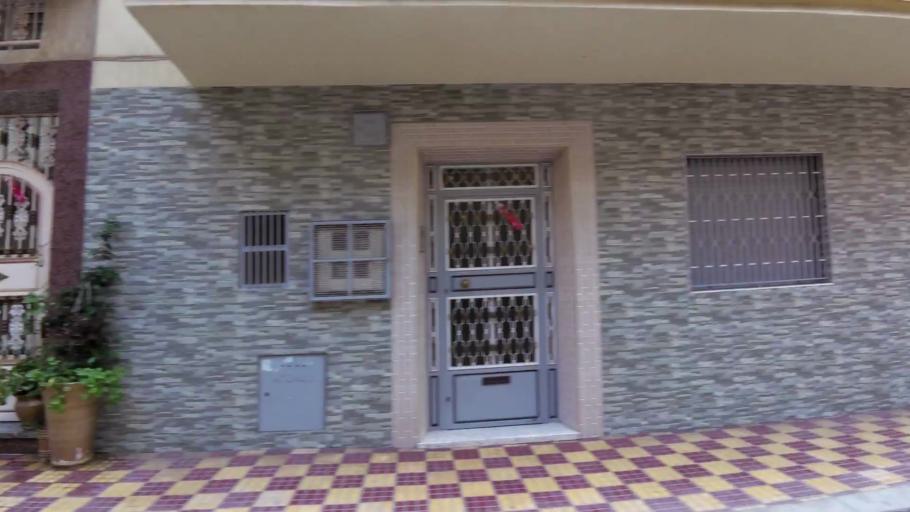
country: MA
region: Tanger-Tetouan
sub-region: Tanger-Assilah
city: Tangier
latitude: 35.7635
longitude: -5.8023
